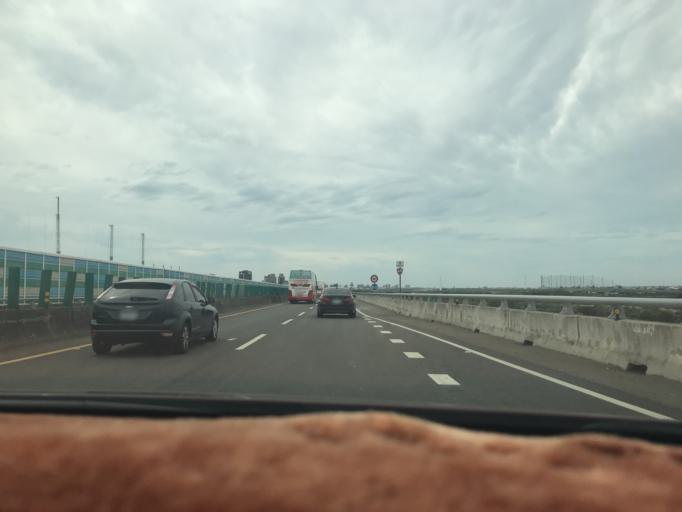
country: TW
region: Taiwan
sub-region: Hsinchu
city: Zhubei
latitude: 24.8216
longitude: 120.9899
